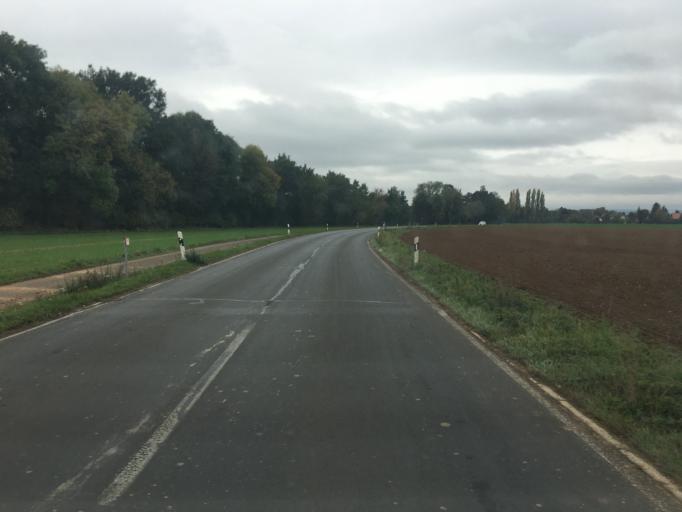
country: DE
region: North Rhine-Westphalia
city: Zulpich
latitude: 50.6770
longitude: 6.6766
